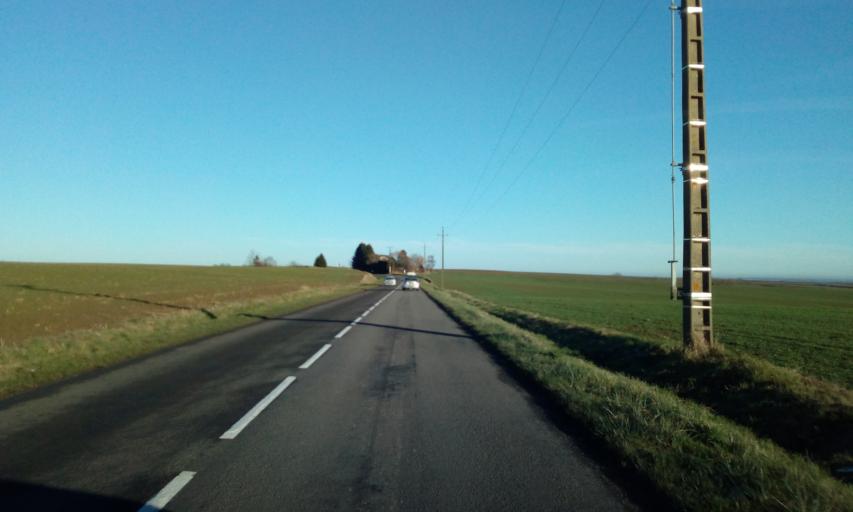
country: FR
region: Picardie
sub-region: Departement de l'Aisne
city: Rozoy-sur-Serre
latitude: 49.6972
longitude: 4.1791
